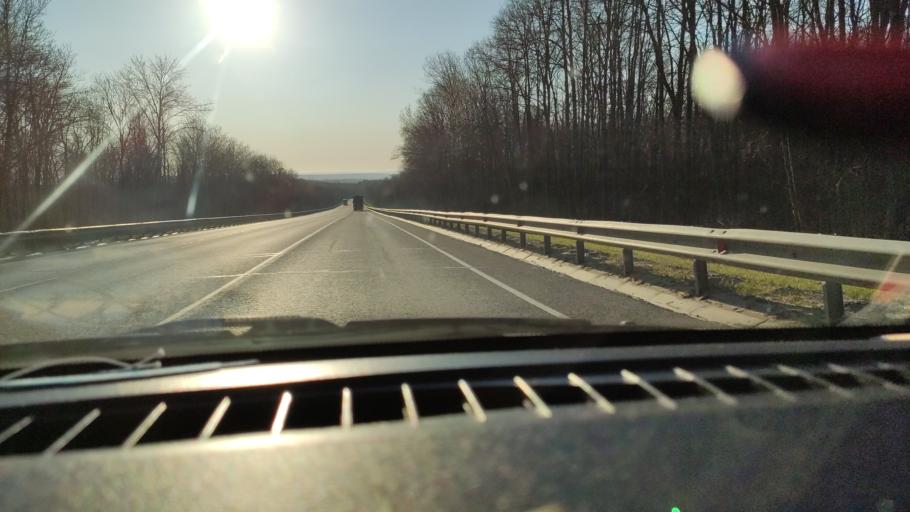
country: RU
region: Saratov
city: Vol'sk
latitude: 52.1072
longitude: 47.4163
